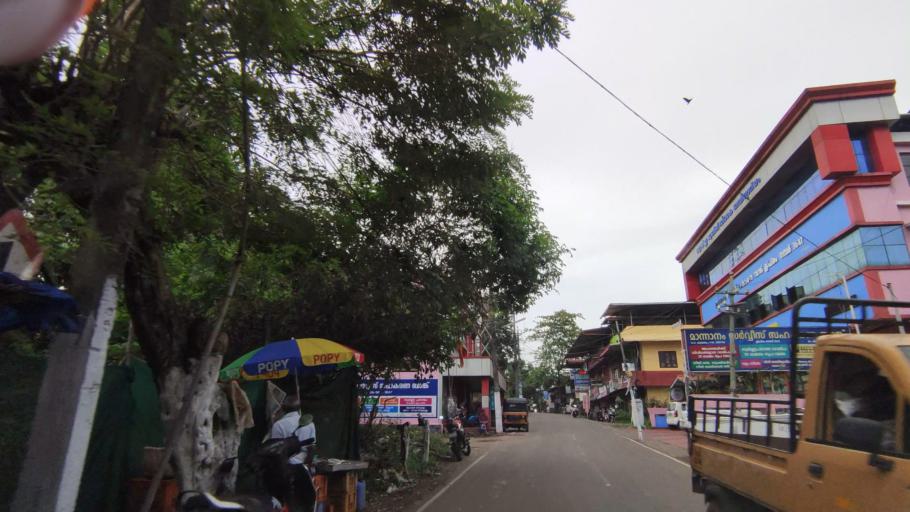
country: IN
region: Kerala
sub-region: Kottayam
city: Kottayam
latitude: 9.6486
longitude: 76.5209
